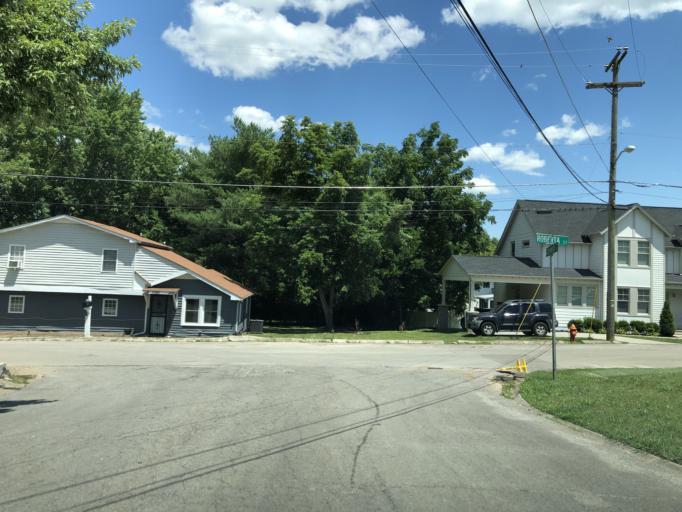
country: US
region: Tennessee
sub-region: Davidson County
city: Nashville
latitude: 36.1877
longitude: -86.7227
